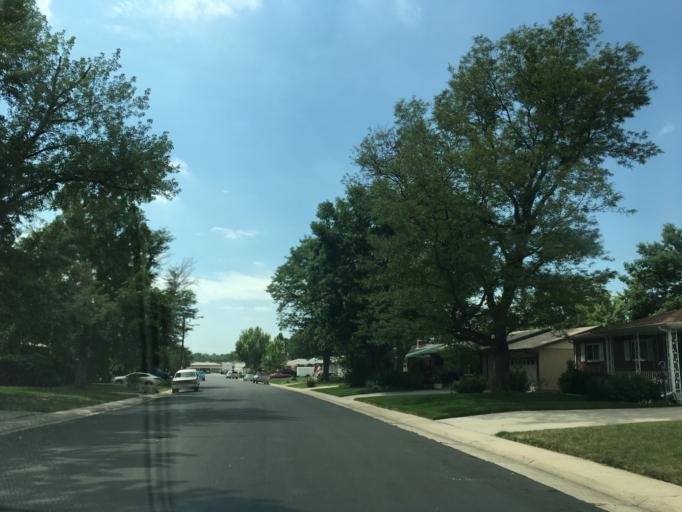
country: US
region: Colorado
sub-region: Arapahoe County
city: Sheridan
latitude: 39.6588
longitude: -105.0498
